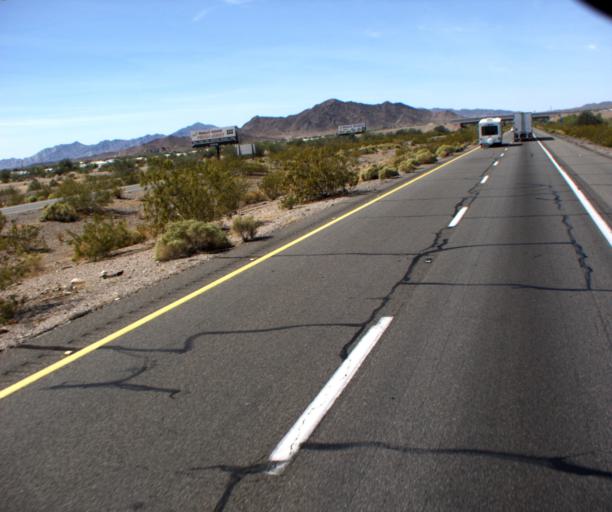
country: US
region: Arizona
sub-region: La Paz County
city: Quartzsite
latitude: 33.6642
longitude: -114.2109
